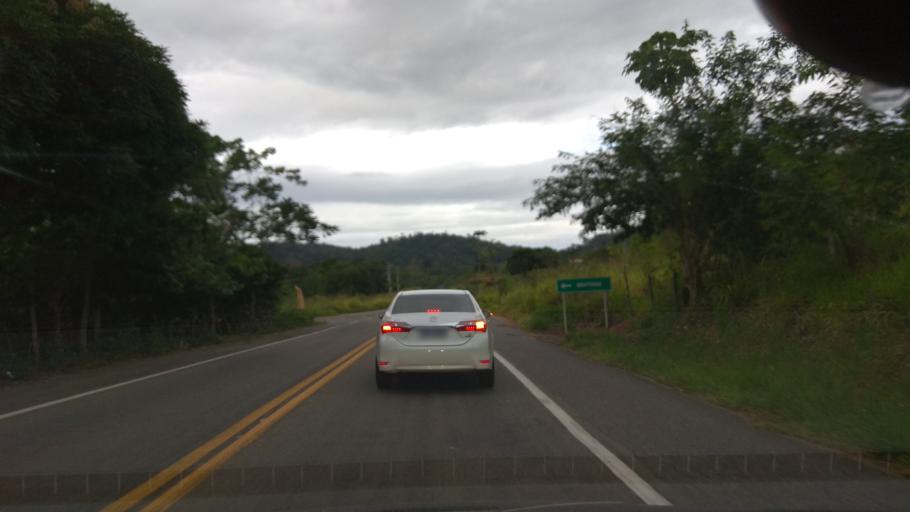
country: BR
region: Bahia
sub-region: Ubata
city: Ubata
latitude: -14.2291
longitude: -39.4475
